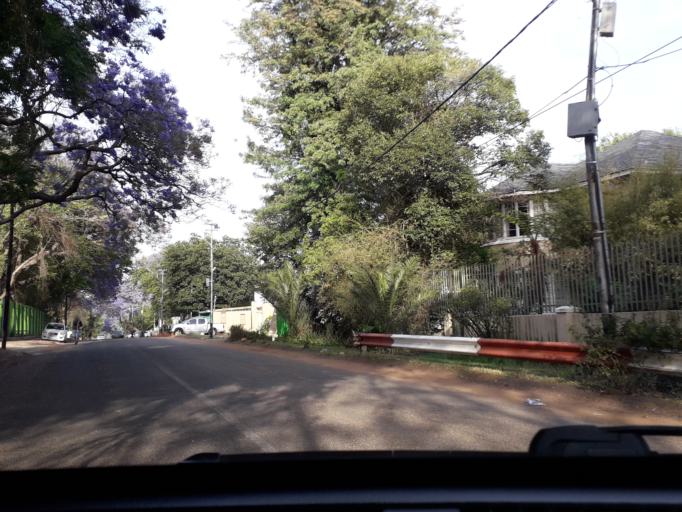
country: ZA
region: Gauteng
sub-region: City of Johannesburg Metropolitan Municipality
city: Johannesburg
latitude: -26.1216
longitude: 28.0799
